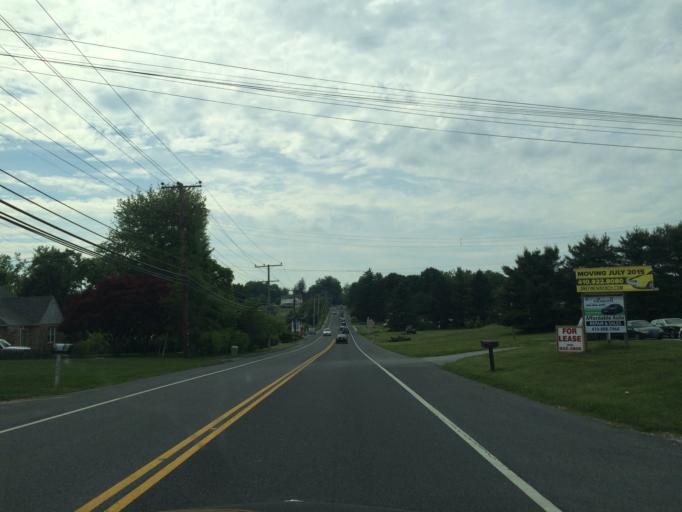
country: US
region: Maryland
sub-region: Baltimore County
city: Randallstown
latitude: 39.3866
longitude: -76.8336
